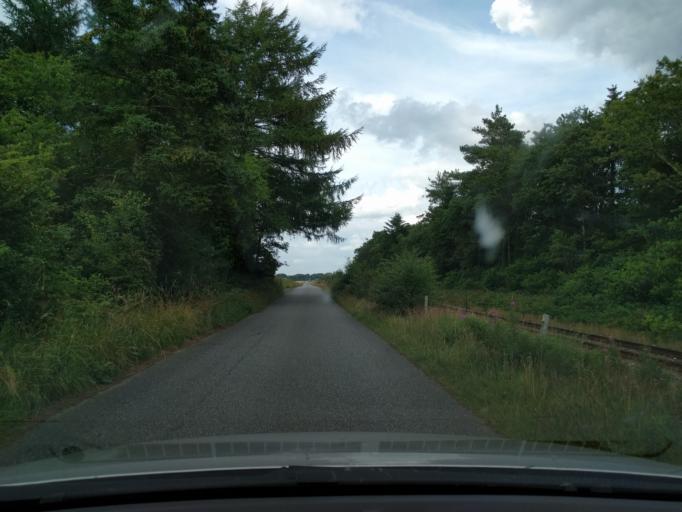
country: DK
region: Central Jutland
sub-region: Herning Kommune
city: Kibaek
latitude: 56.0778
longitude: 8.8958
